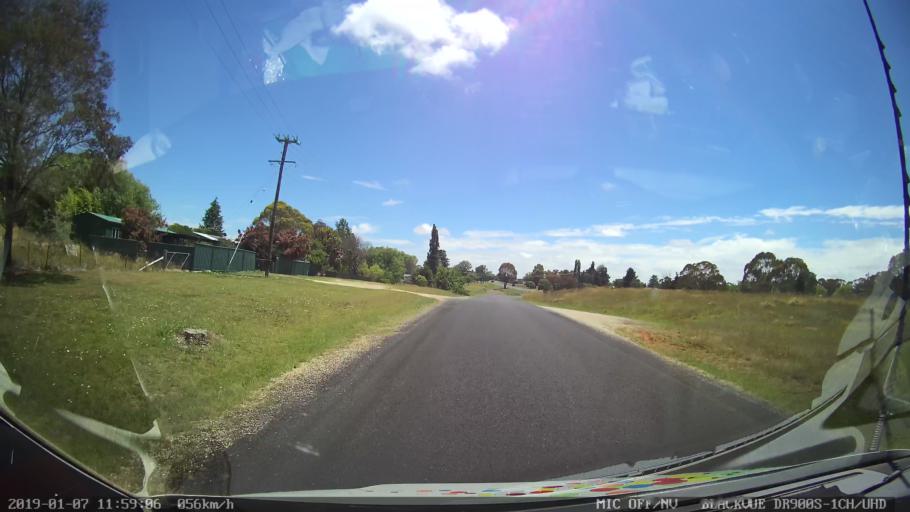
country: AU
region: New South Wales
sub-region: Guyra
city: Guyra
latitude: -30.2463
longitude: 151.6691
